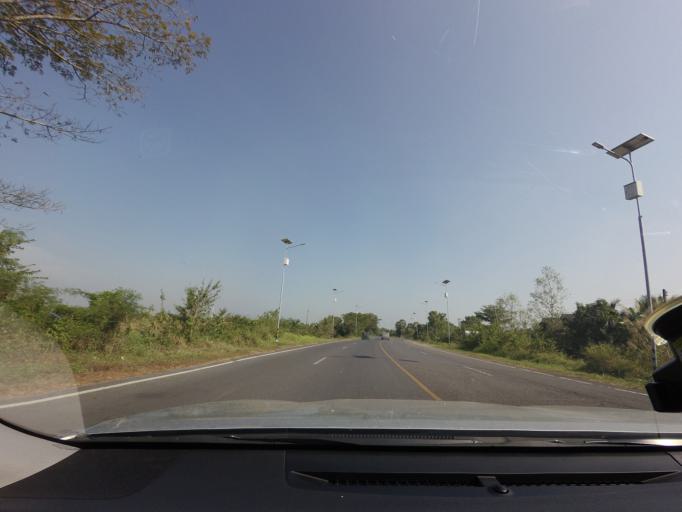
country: TH
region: Nakhon Si Thammarat
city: Nakhon Si Thammarat
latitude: 8.4952
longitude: 99.9726
